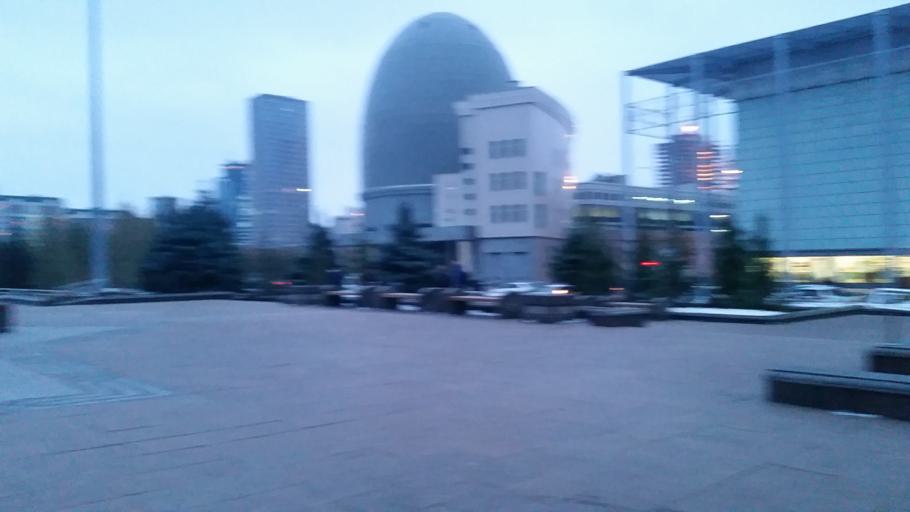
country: KZ
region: Astana Qalasy
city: Astana
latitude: 51.1289
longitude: 71.4260
